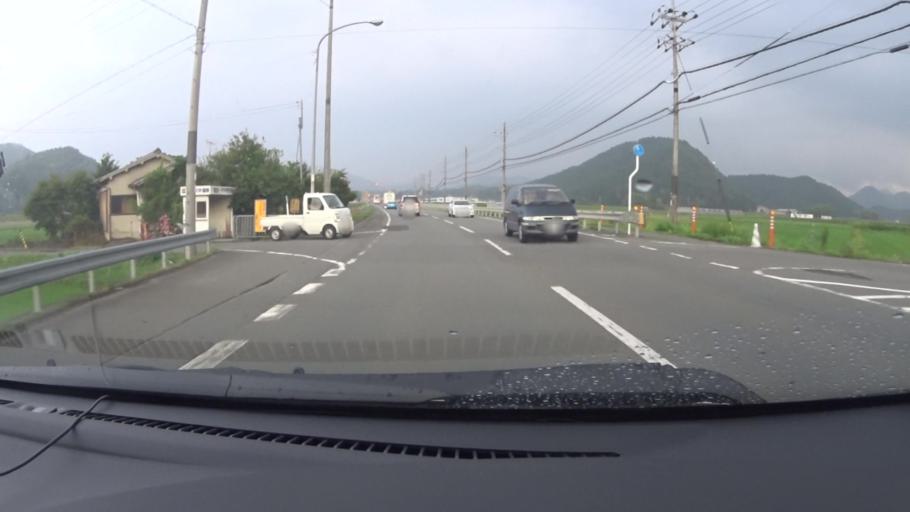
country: JP
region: Kyoto
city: Ayabe
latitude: 35.1877
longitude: 135.4170
